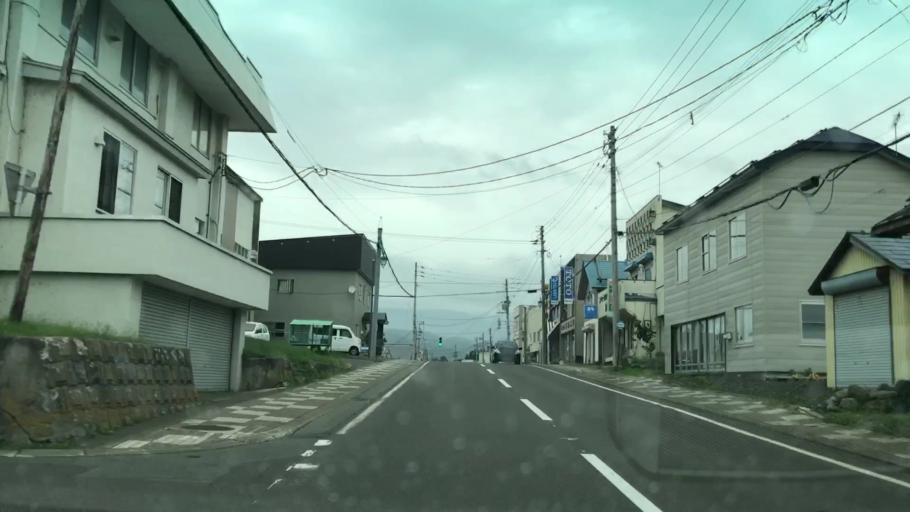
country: JP
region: Hokkaido
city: Niseko Town
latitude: 42.8040
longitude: 140.5270
